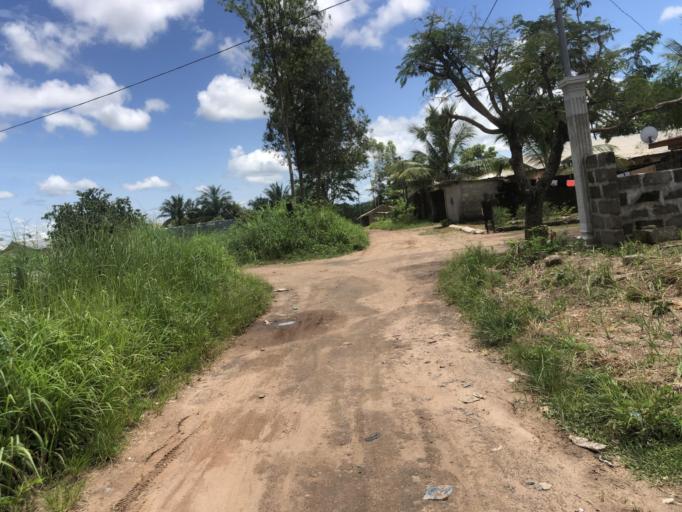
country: SL
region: Northern Province
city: Makeni
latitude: 8.8583
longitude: -12.0444
